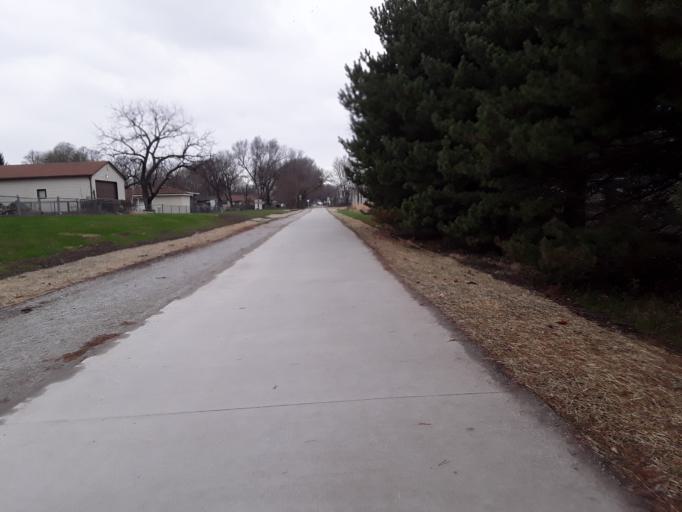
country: US
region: Nebraska
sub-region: Lancaster County
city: Lincoln
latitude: 40.8514
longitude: -96.6315
